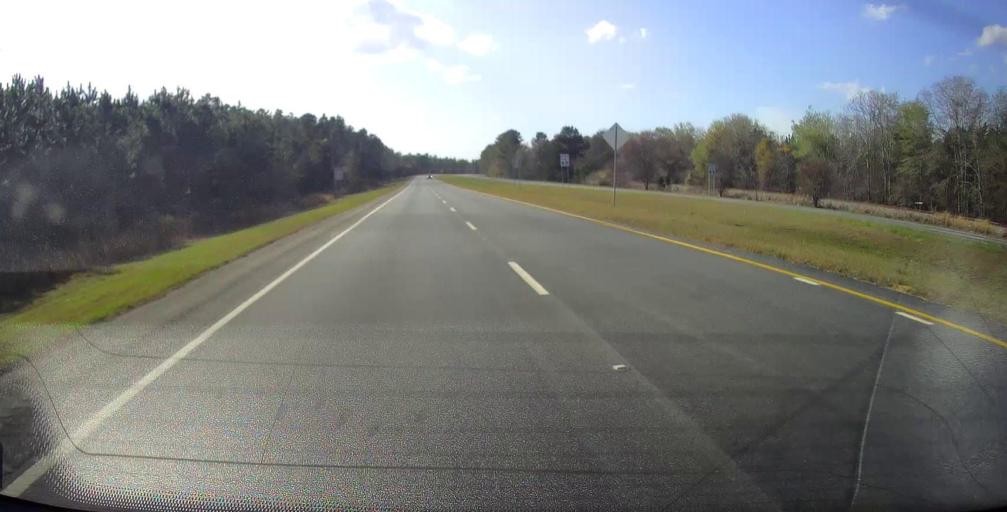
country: US
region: Georgia
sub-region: Dodge County
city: Eastman
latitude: 32.1080
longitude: -83.0859
